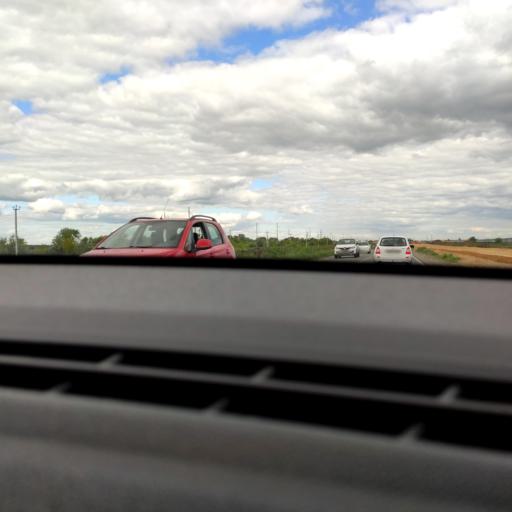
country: RU
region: Samara
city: Podstepki
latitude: 53.5635
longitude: 49.1713
